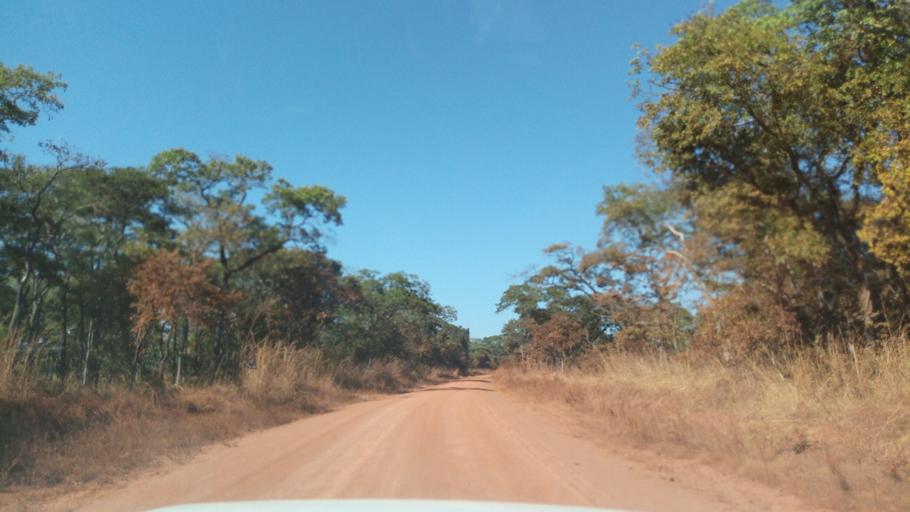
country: ZM
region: Luapula
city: Mwense
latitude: -10.7186
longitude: 28.3623
